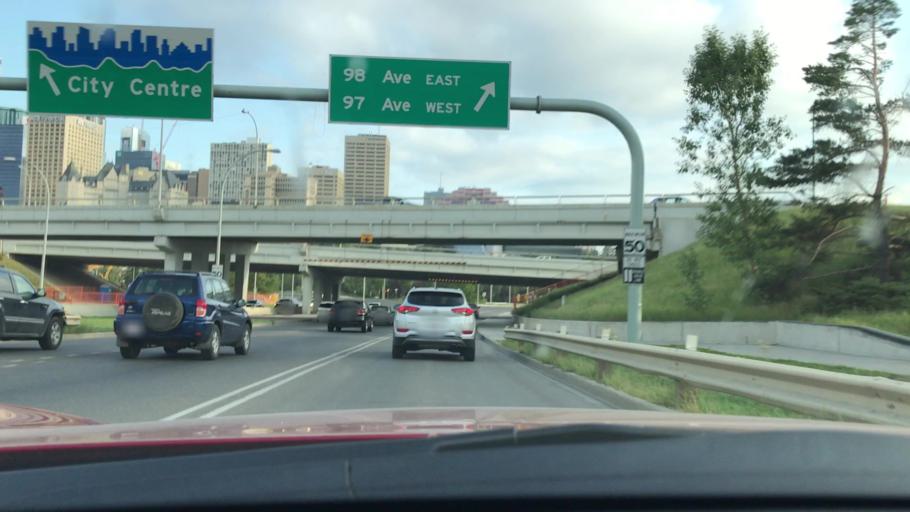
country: CA
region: Alberta
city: Edmonton
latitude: 53.5355
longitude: -113.4835
